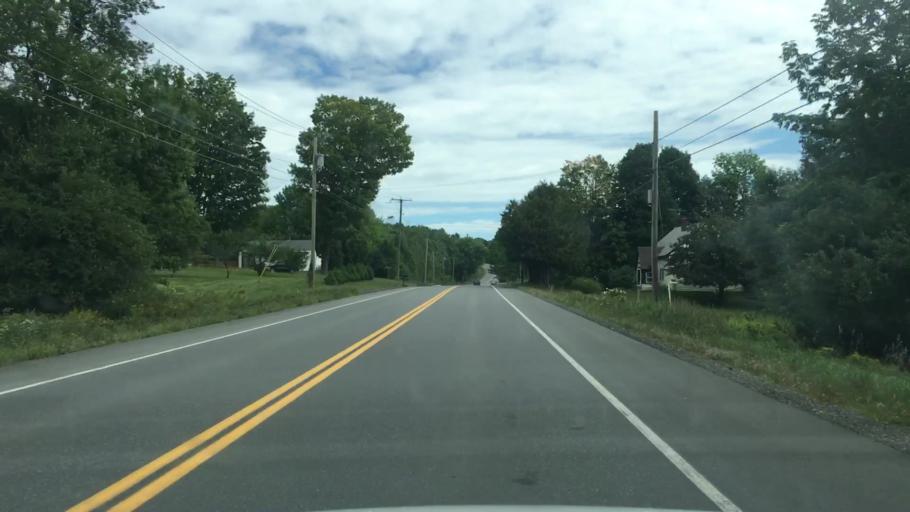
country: US
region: Maine
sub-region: Piscataquis County
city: Milo
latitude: 45.2419
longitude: -69.0282
